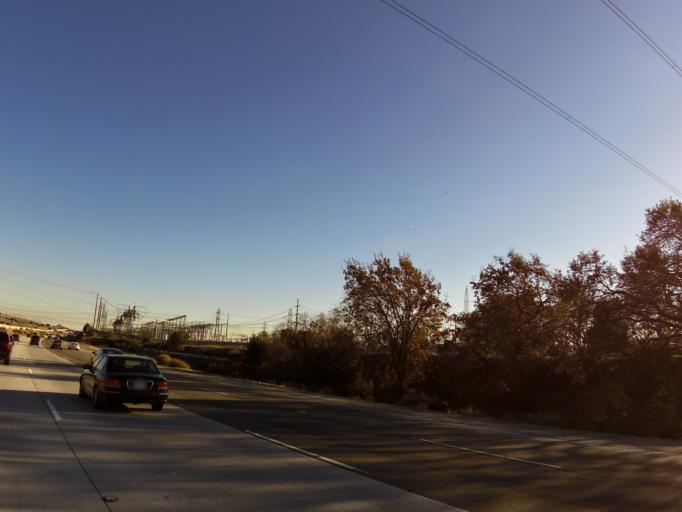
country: US
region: California
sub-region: Santa Clara County
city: Seven Trees
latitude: 37.2283
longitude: -121.7452
